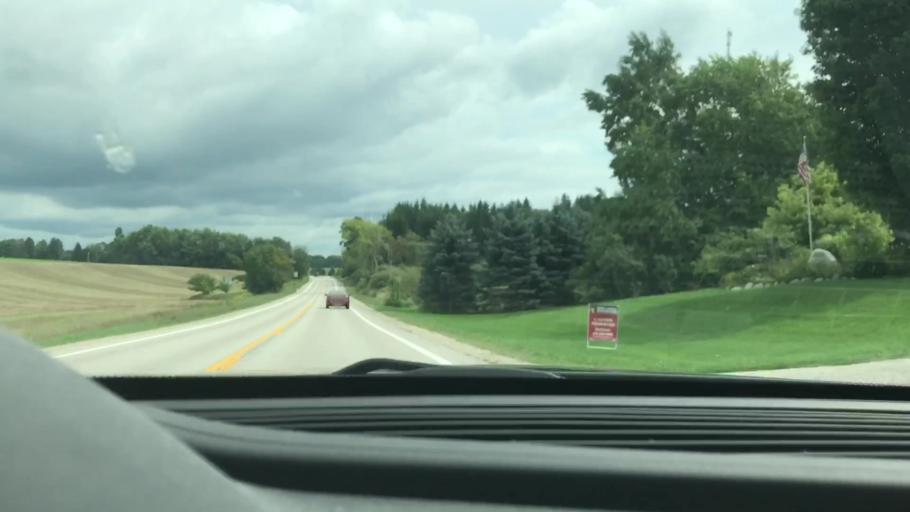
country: US
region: Michigan
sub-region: Antrim County
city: Bellaire
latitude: 45.0963
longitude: -85.2981
